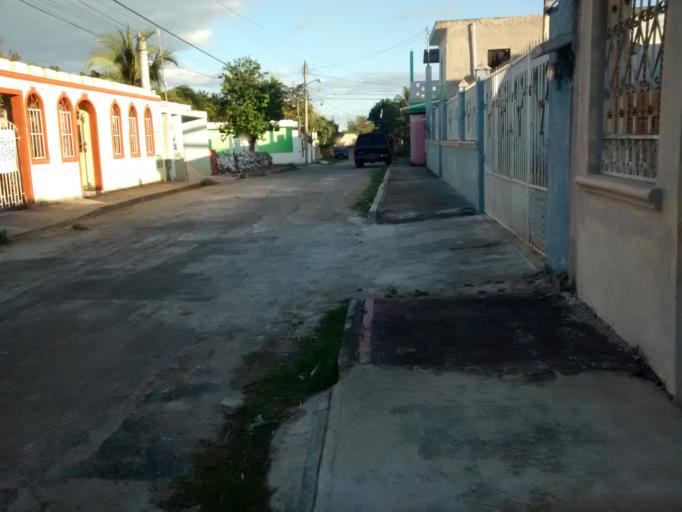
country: MX
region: Yucatan
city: Valladolid
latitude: 20.6851
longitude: -88.1886
